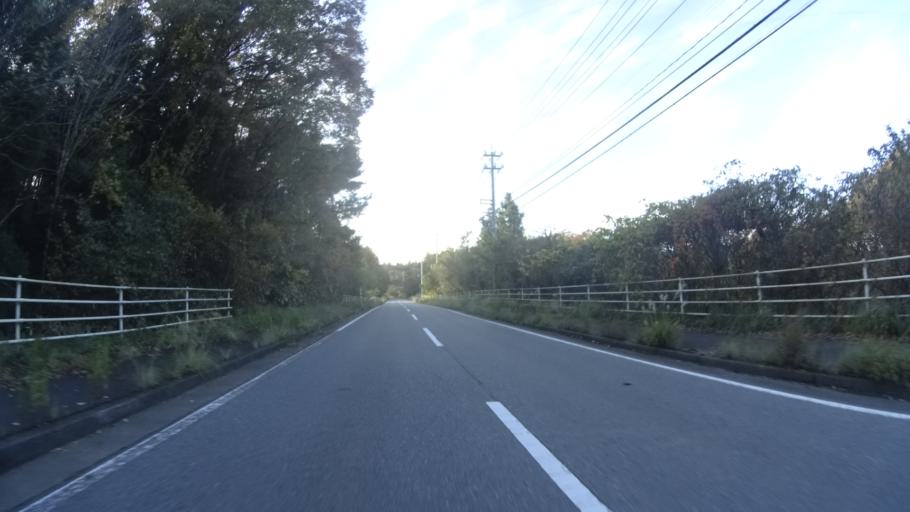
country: JP
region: Ishikawa
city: Hakui
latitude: 37.0643
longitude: 136.7729
